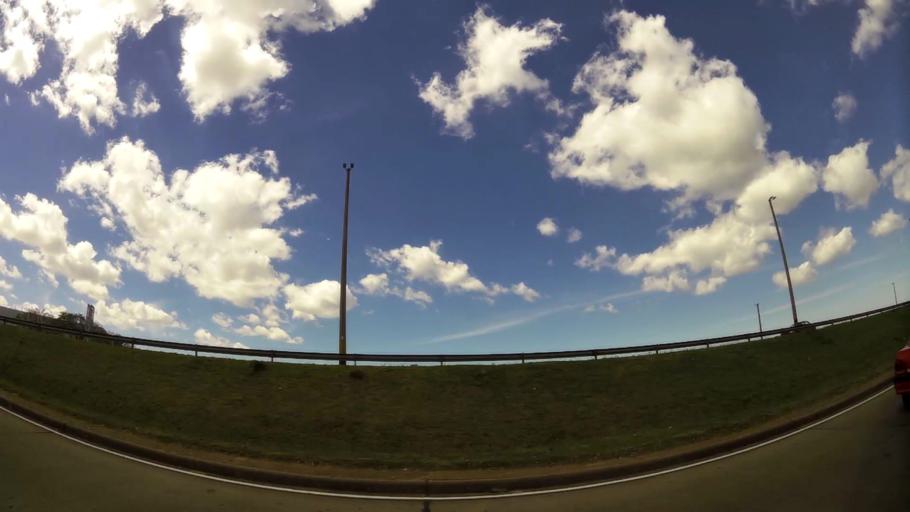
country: UY
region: Montevideo
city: Montevideo
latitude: -34.8740
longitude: -56.2102
